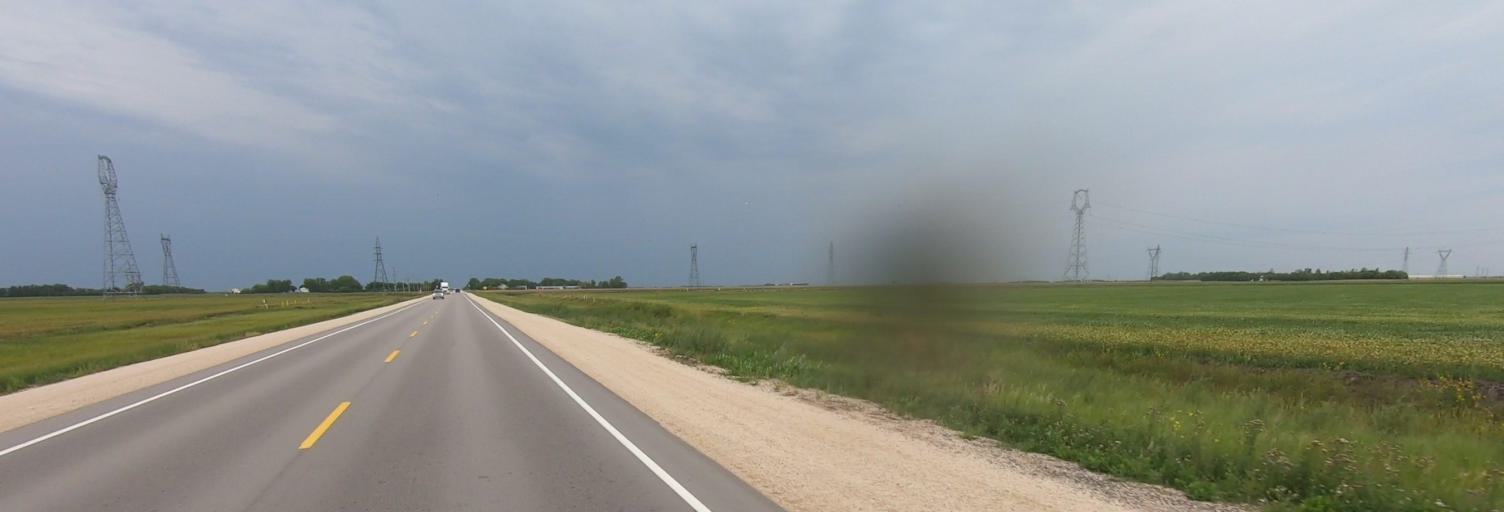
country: CA
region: Manitoba
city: Headingley
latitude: 49.7684
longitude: -97.3495
